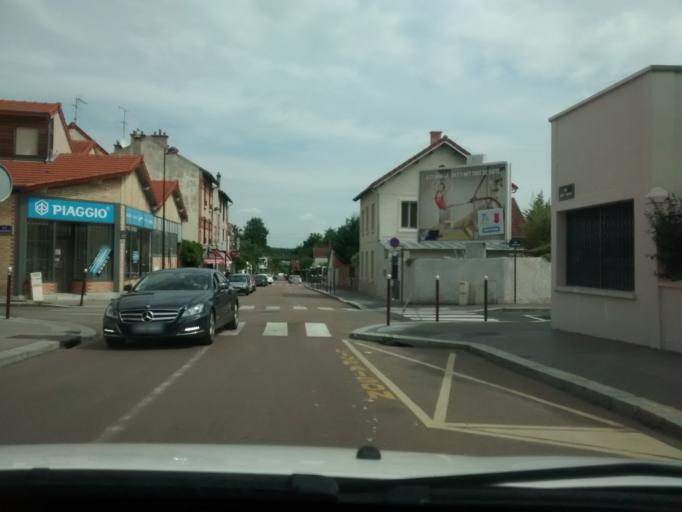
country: FR
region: Ile-de-France
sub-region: Departement des Yvelines
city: Viroflay
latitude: 48.7931
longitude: 2.1484
